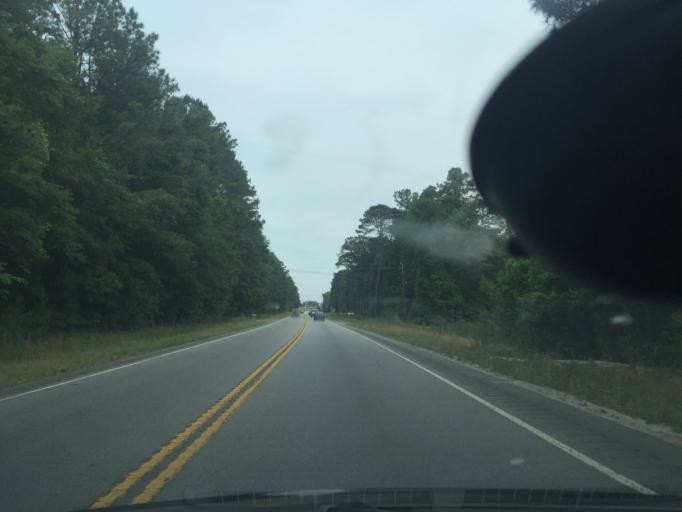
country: US
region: Georgia
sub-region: Chatham County
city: Georgetown
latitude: 32.0101
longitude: -81.2937
